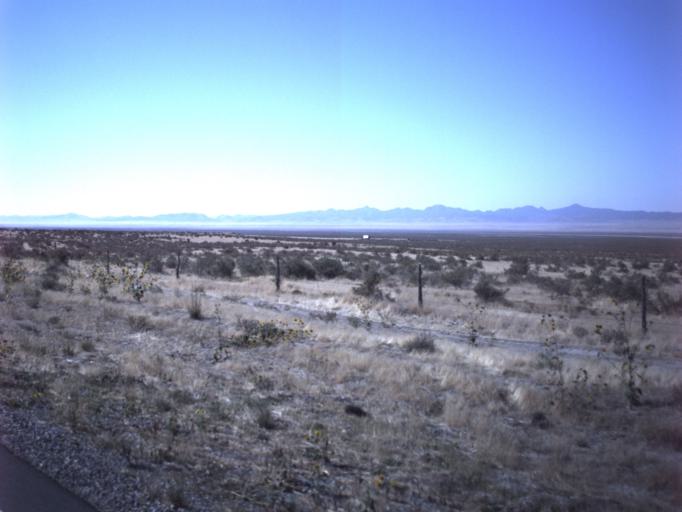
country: US
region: Utah
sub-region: Tooele County
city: Grantsville
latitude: 40.5124
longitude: -112.7477
